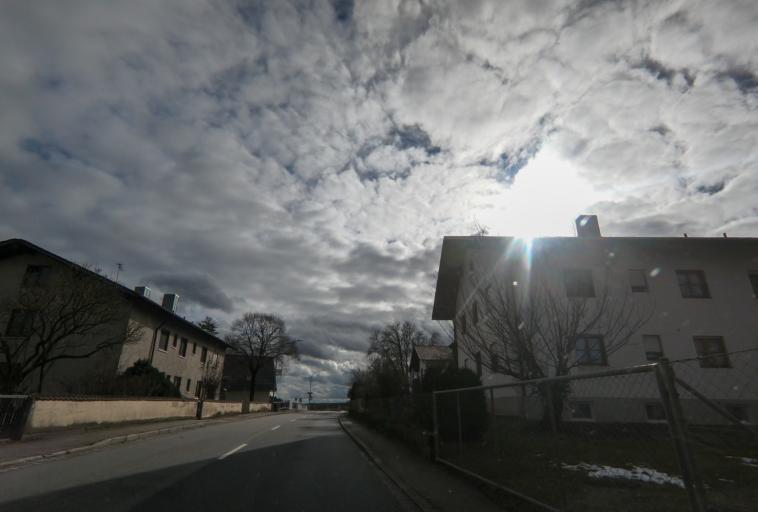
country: DE
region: Bavaria
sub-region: Lower Bavaria
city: Essenbach
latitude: 48.6376
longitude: 12.2106
